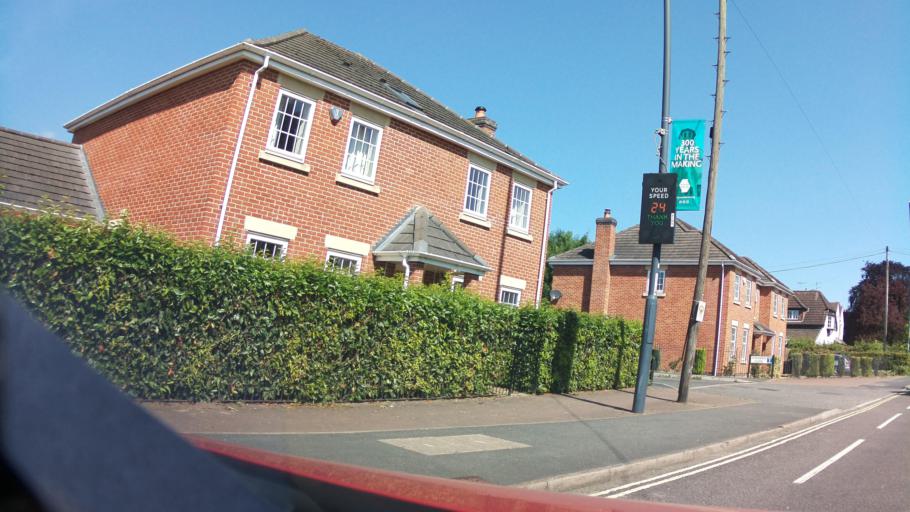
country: GB
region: England
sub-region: Derby
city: Derby
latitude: 52.9430
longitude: -1.4844
